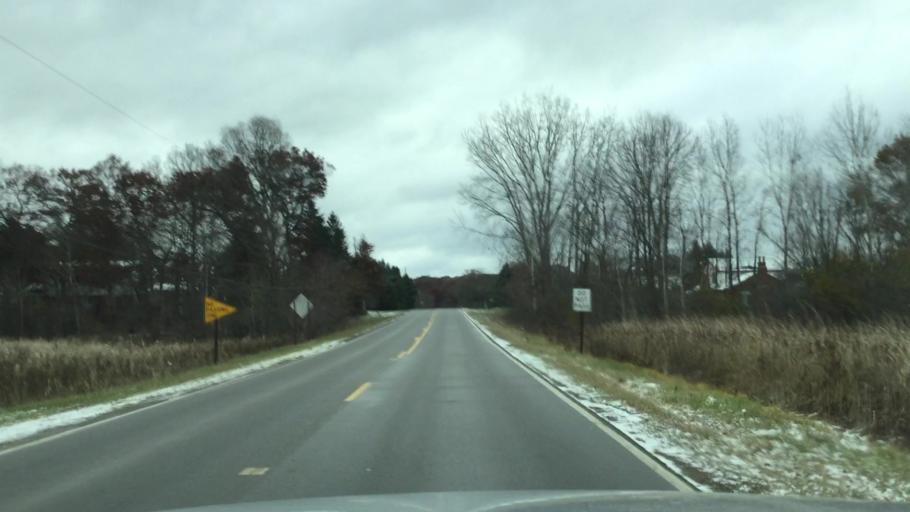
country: US
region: Michigan
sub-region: Livingston County
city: Brighton
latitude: 42.5388
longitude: -83.7229
